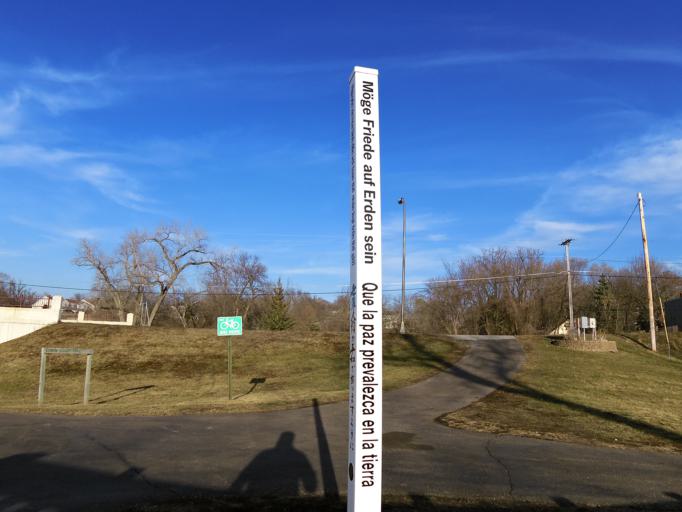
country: US
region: Minnesota
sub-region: Goodhue County
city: Cannon Falls
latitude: 44.5100
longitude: -92.9064
